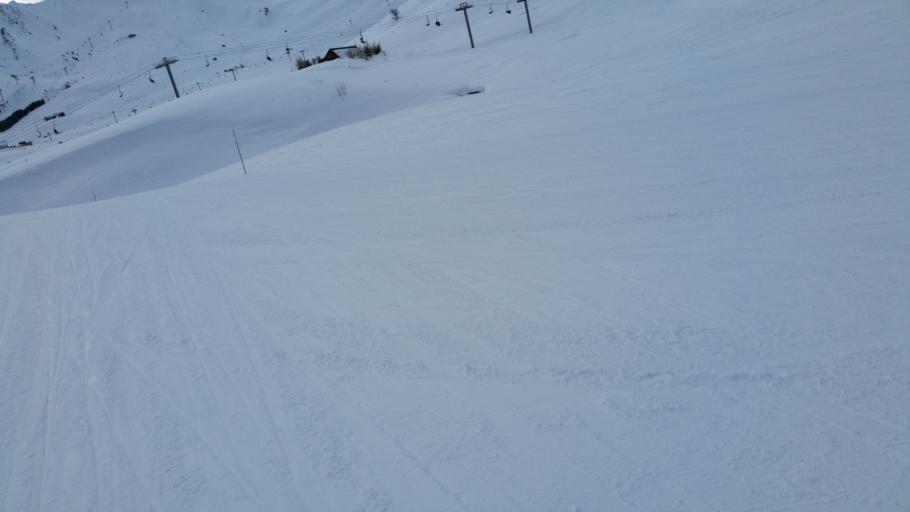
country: FR
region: Rhone-Alpes
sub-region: Departement de la Savoie
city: Saint-Jean-de-Maurienne
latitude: 45.2641
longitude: 6.2673
